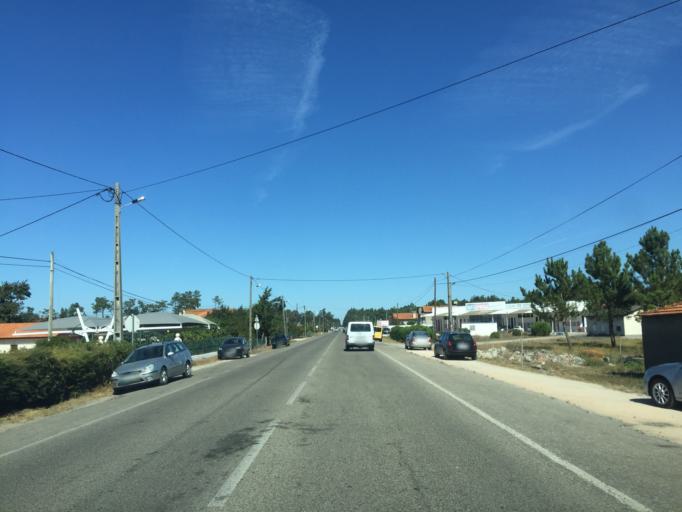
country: PT
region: Coimbra
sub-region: Figueira da Foz
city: Alhadas
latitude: 40.2818
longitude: -8.7708
